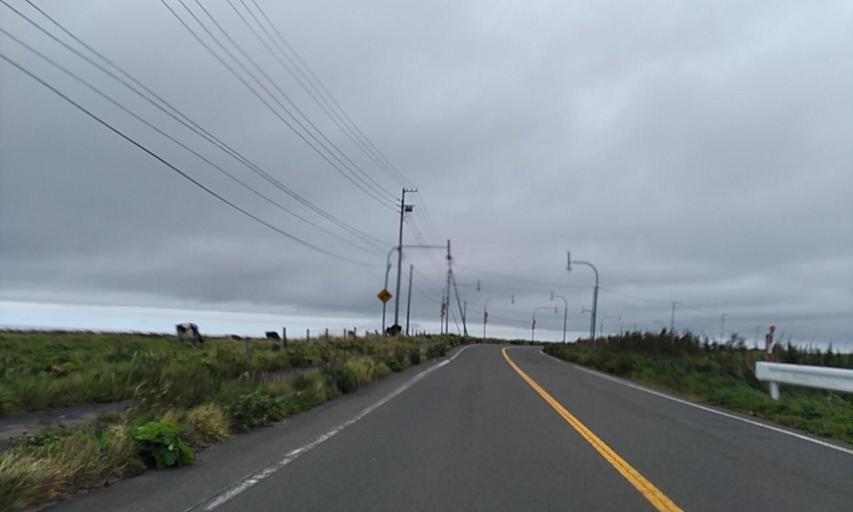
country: JP
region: Hokkaido
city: Nemuro
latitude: 43.3566
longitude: 145.6126
